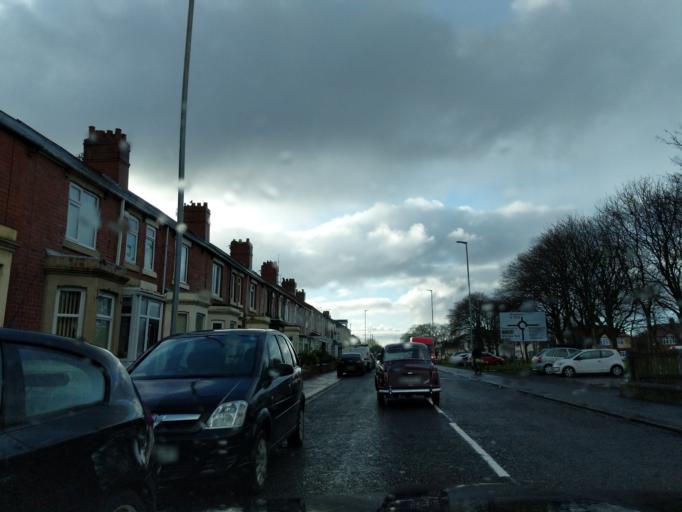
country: GB
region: England
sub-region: Northumberland
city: Blyth
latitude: 55.1198
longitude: -1.5104
